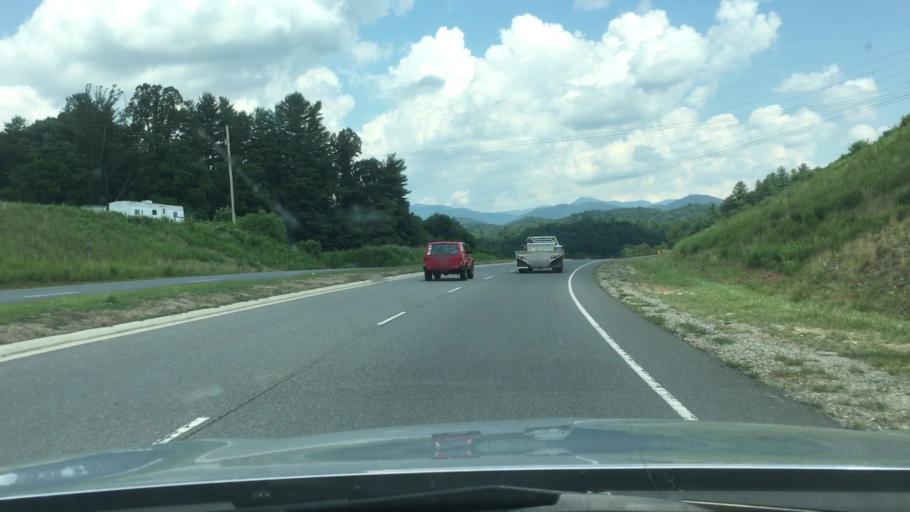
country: US
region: North Carolina
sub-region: Madison County
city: Mars Hill
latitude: 35.8398
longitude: -82.5160
